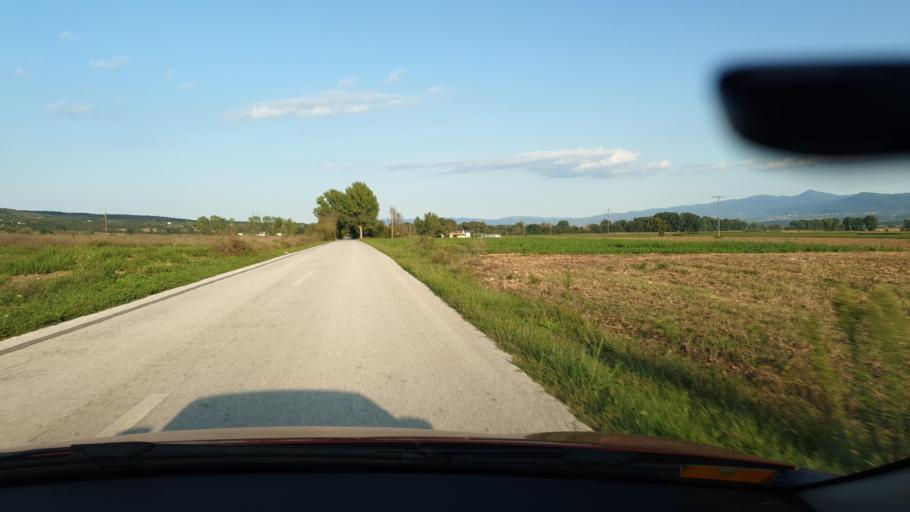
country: GR
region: Central Macedonia
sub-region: Nomos Chalkidikis
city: Galatista
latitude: 40.5643
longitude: 23.3231
